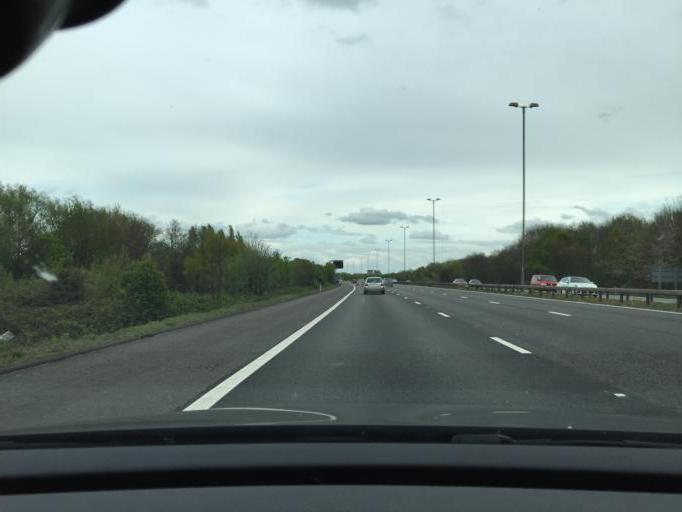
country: GB
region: England
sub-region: West Berkshire
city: Calcot
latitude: 51.4282
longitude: -1.0438
